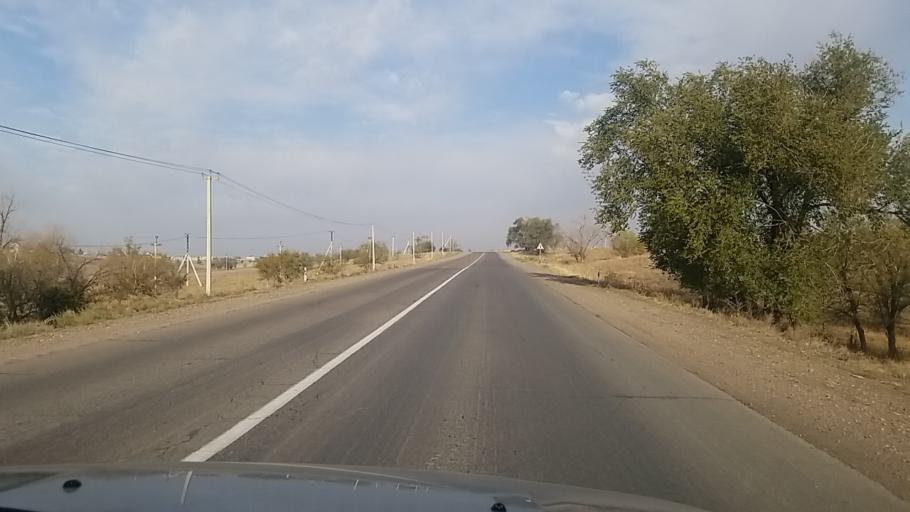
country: KZ
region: Almaty Oblysy
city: Burunday
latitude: 43.4723
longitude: 76.6960
